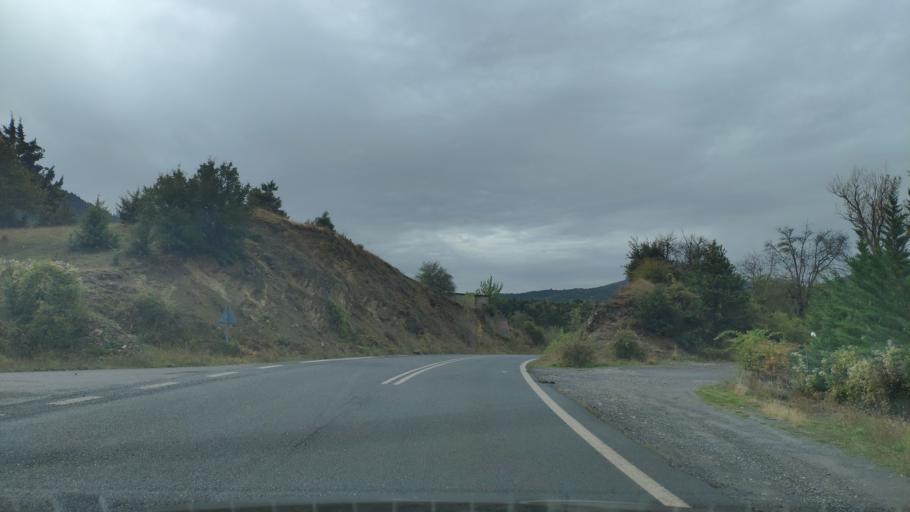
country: GR
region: Peloponnese
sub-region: Nomos Arkadias
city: Dimitsana
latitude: 37.6532
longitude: 22.1881
